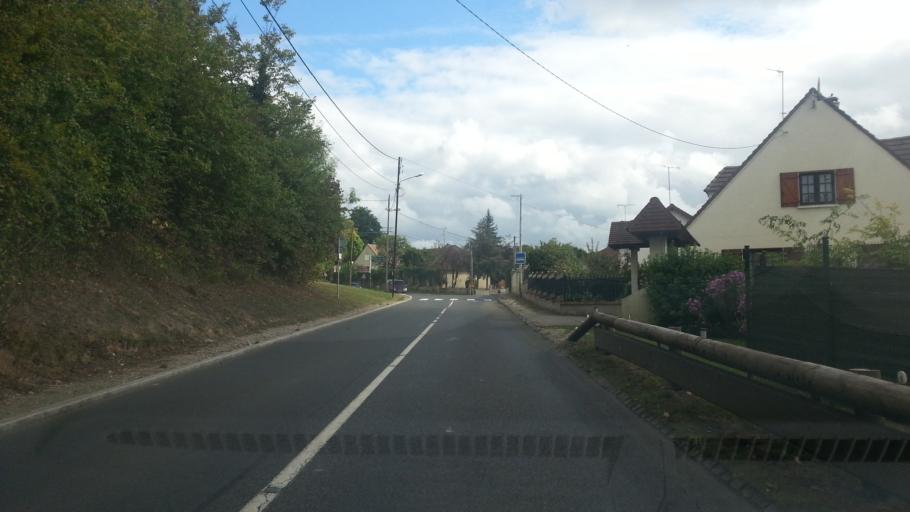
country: FR
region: Picardie
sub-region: Departement de l'Oise
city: Gouvieux
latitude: 49.1997
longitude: 2.4303
